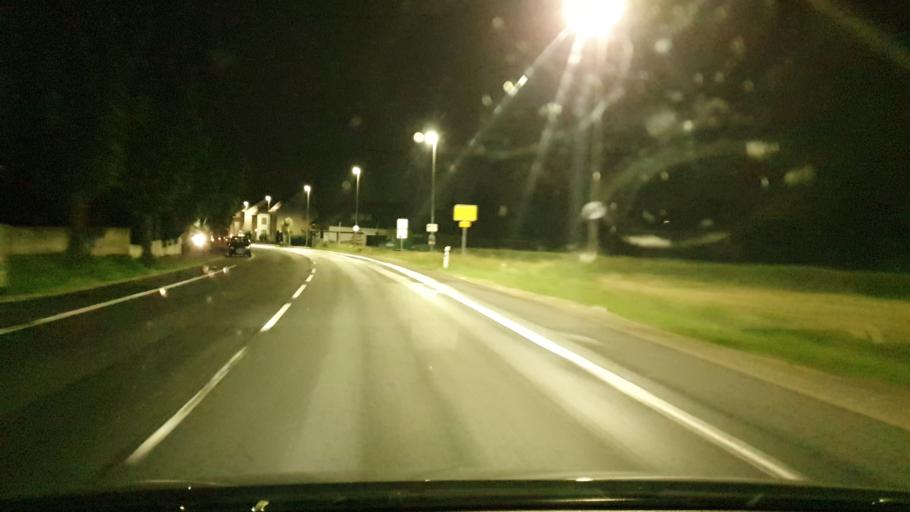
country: DE
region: Hesse
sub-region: Regierungsbezirk Darmstadt
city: Florsheim
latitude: 50.0486
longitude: 8.4338
